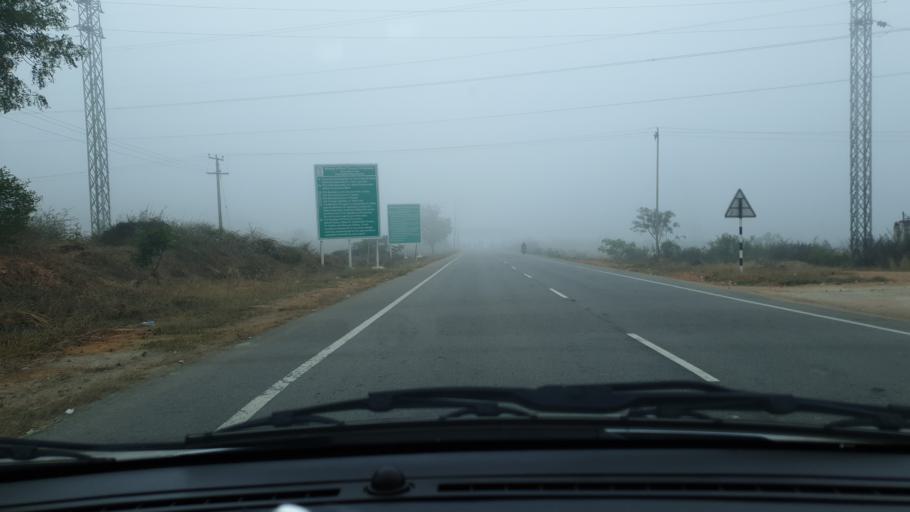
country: IN
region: Telangana
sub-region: Nalgonda
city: Devarkonda
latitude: 16.6148
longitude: 78.6747
